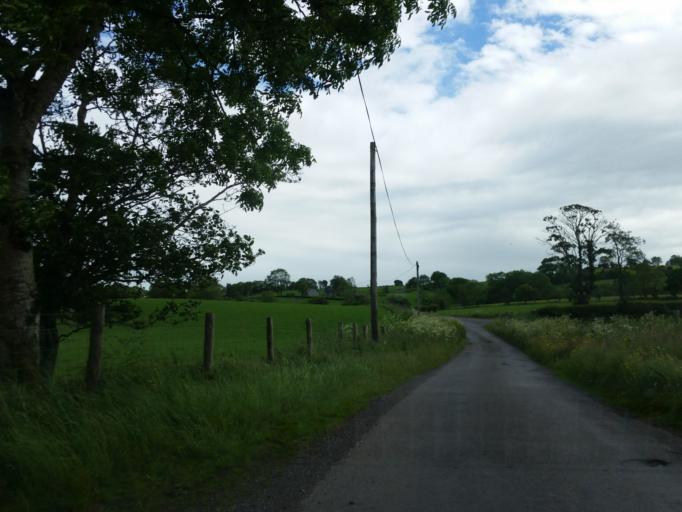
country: GB
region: Northern Ireland
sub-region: Omagh District
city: Omagh
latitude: 54.5480
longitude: -7.1338
